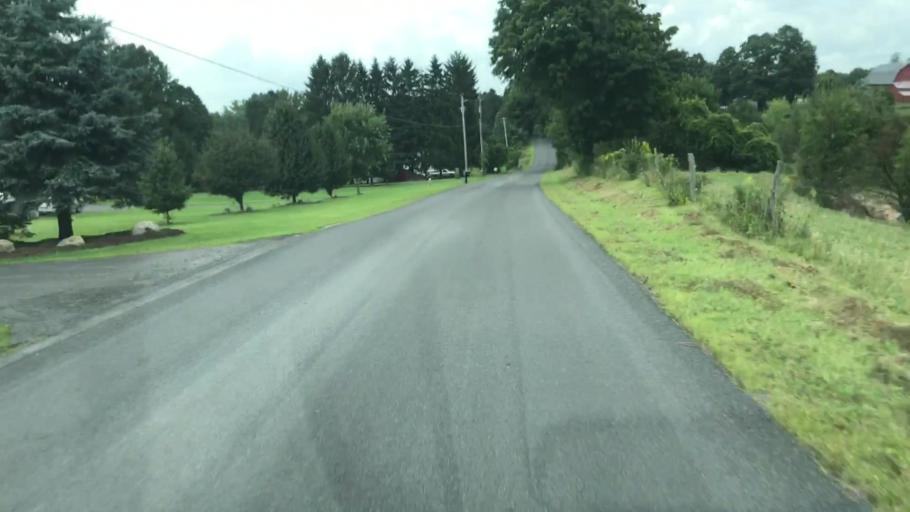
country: US
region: New York
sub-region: Cayuga County
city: Auburn
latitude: 42.9781
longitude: -76.5101
